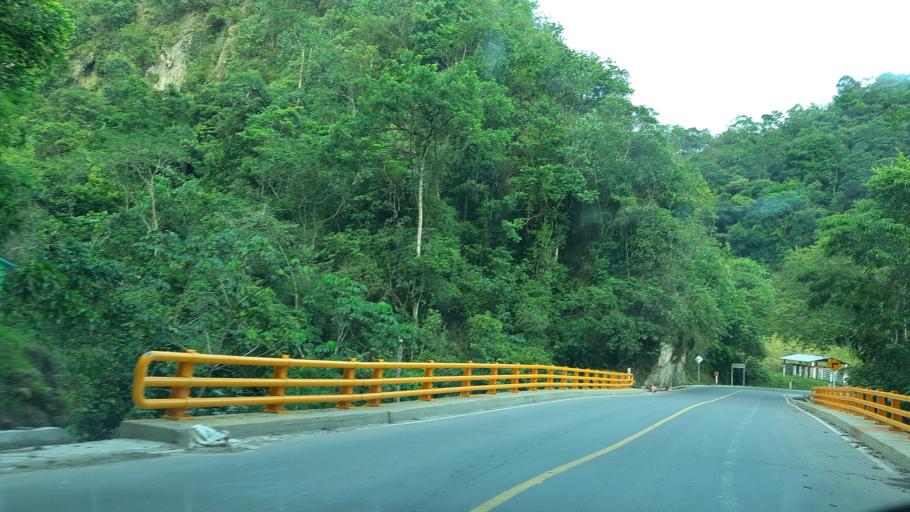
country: CO
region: Boyaca
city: San Luis de Gaceno
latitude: 4.8351
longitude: -73.2079
